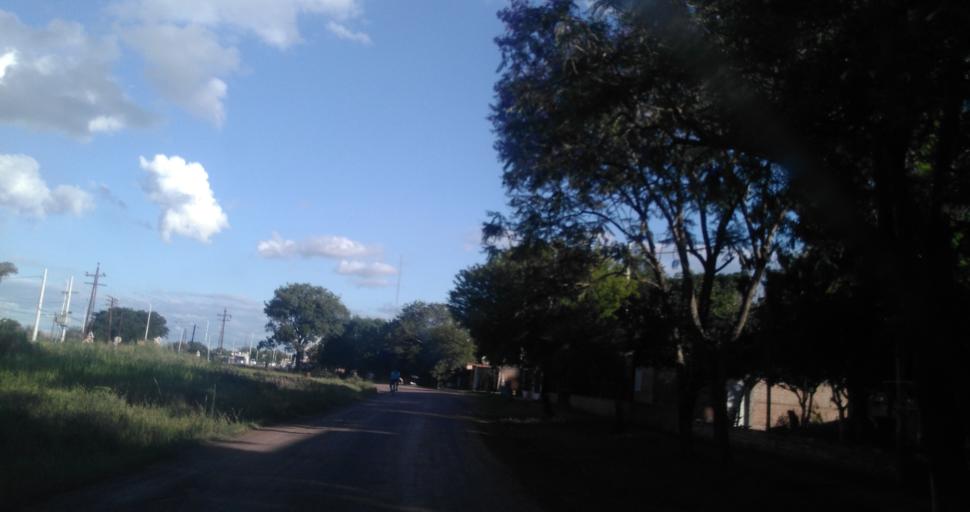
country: AR
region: Chaco
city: Fontana
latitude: -27.4220
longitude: -59.0345
